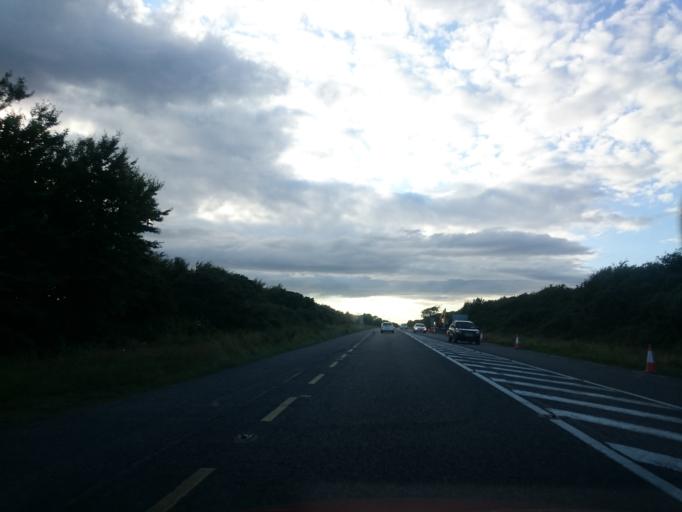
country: IE
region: Leinster
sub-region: Loch Garman
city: Loch Garman
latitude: 52.3114
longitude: -6.4866
